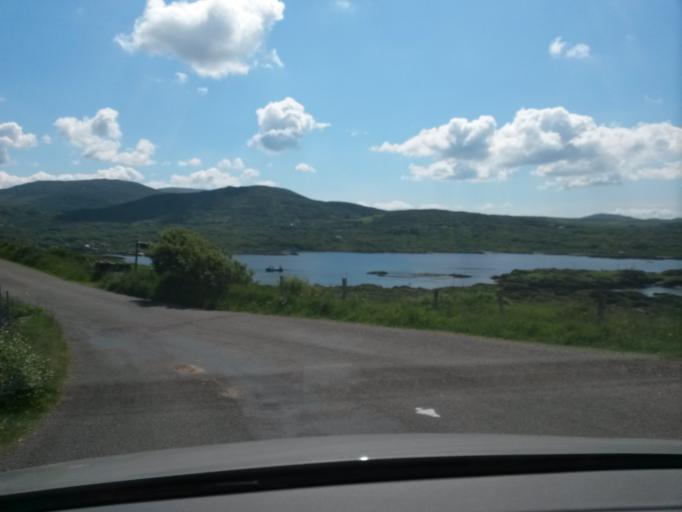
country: IE
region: Munster
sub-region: Ciarrai
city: Cahersiveen
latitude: 51.7159
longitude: -9.9630
